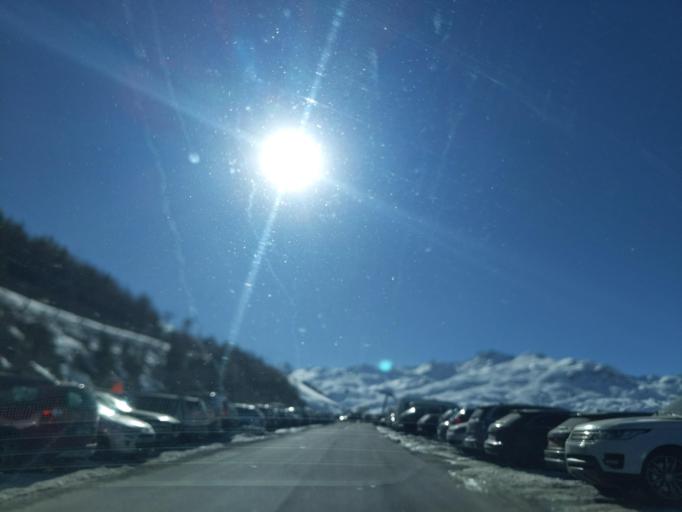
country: FR
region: Rhone-Alpes
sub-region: Departement de la Savoie
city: Val Thorens
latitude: 45.3209
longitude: 6.5389
